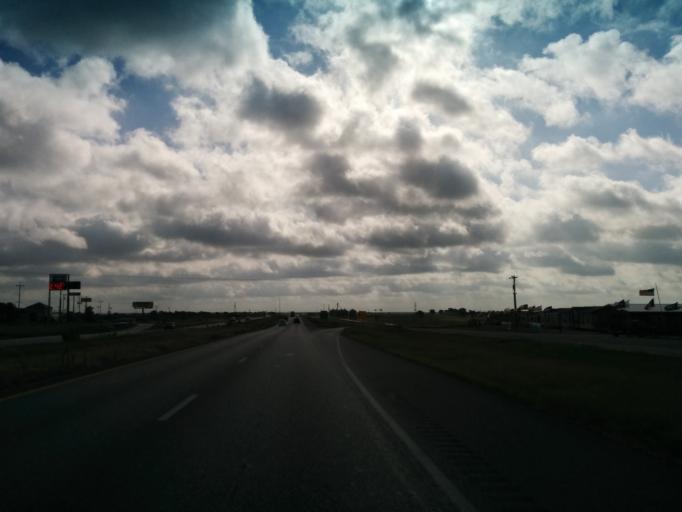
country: US
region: Texas
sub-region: Guadalupe County
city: McQueeney
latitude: 29.5391
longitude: -98.0763
